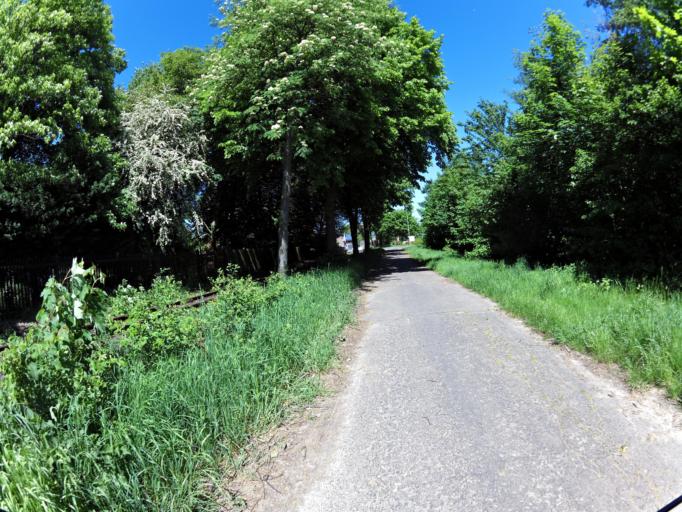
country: DE
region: North Rhine-Westphalia
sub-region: Regierungsbezirk Koln
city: Gangelt
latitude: 51.0042
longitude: 6.0607
